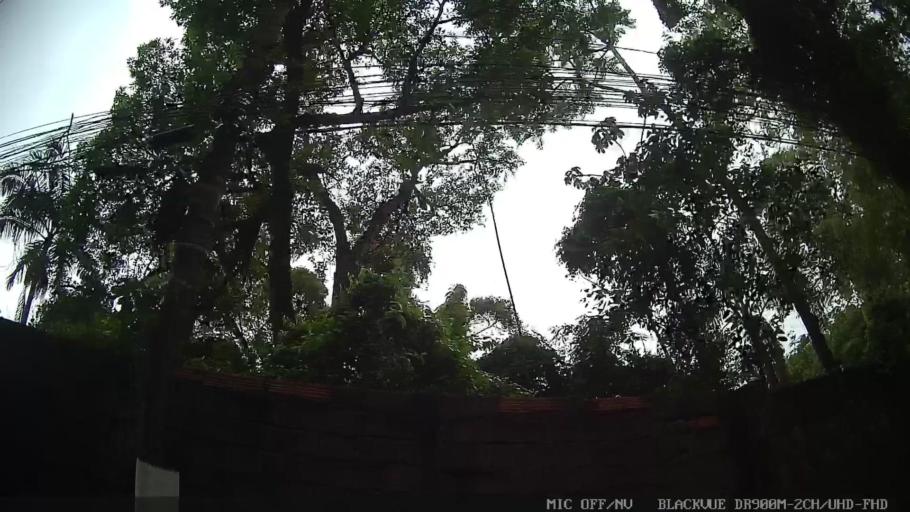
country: BR
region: Sao Paulo
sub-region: Osasco
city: Osasco
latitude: -23.4583
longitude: -46.7557
